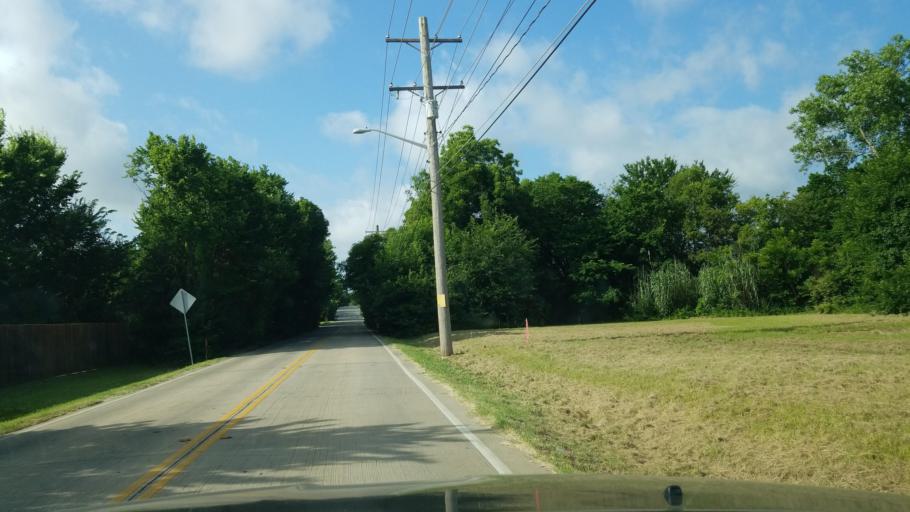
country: US
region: Texas
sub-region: Denton County
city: Denton
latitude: 33.2325
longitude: -97.0989
